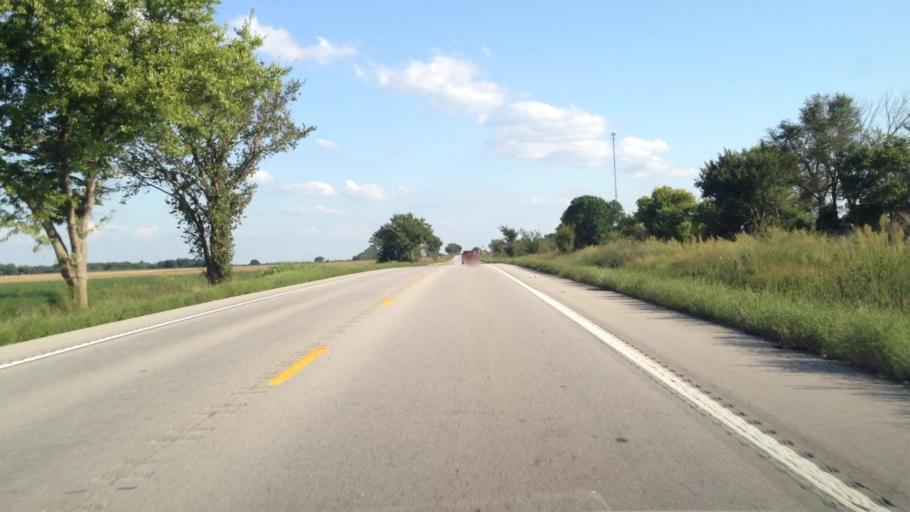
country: US
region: Missouri
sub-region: Jasper County
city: Carl Junction
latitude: 37.2679
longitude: -94.5979
